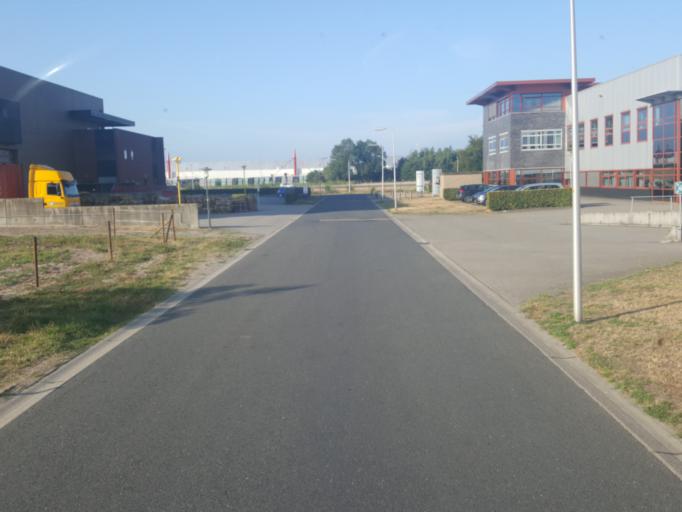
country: NL
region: Overijssel
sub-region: Gemeente Hengelo
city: Hengelo
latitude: 52.2112
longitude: 6.8168
